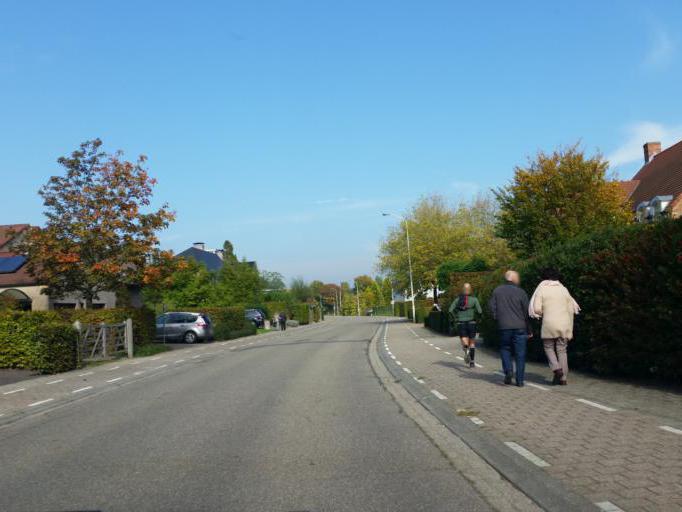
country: BE
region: Flanders
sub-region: Provincie Antwerpen
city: Aartselaar
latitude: 51.1294
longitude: 4.4018
